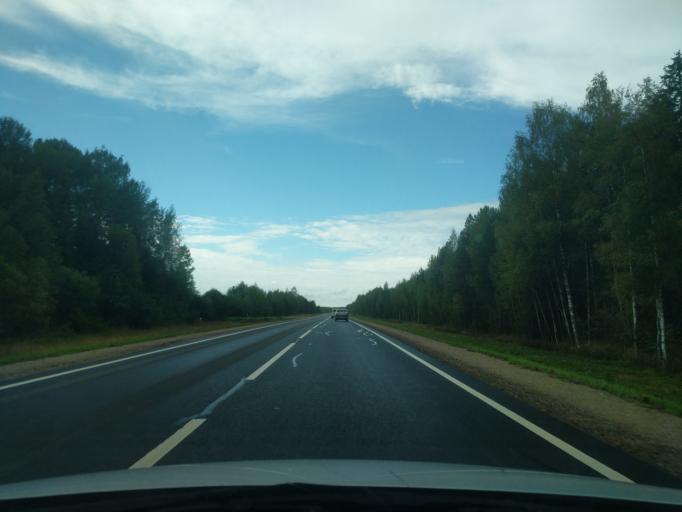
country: RU
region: Kostroma
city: Ostrovskoye
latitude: 57.8141
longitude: 42.0046
